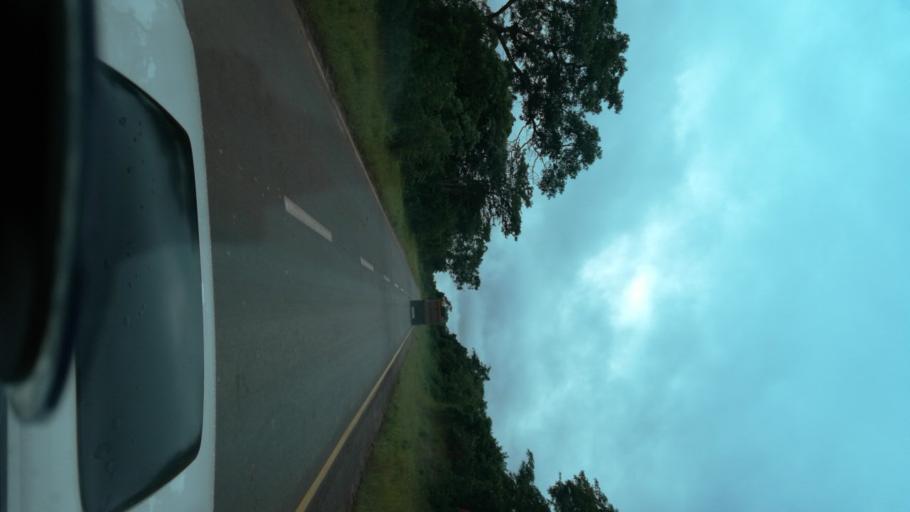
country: CD
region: Katanga
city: Lubumbashi
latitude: -11.1590
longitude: 27.9396
